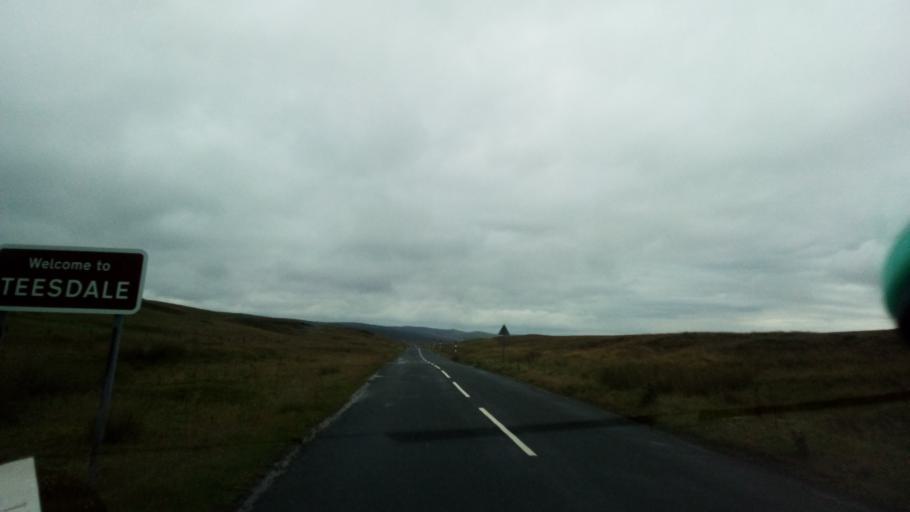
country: GB
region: England
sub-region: County Durham
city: Holwick
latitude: 54.5747
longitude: -2.2605
